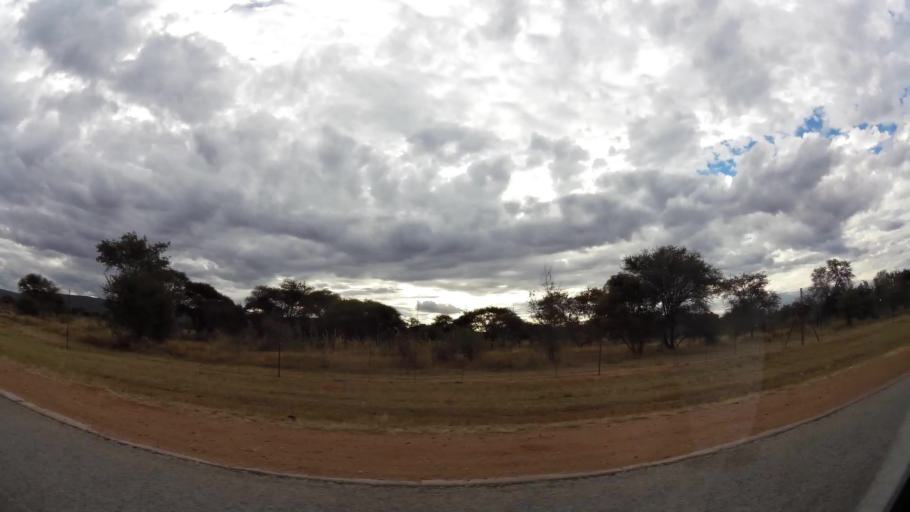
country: ZA
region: Limpopo
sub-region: Waterberg District Municipality
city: Modimolle
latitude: -24.5377
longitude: 28.6963
